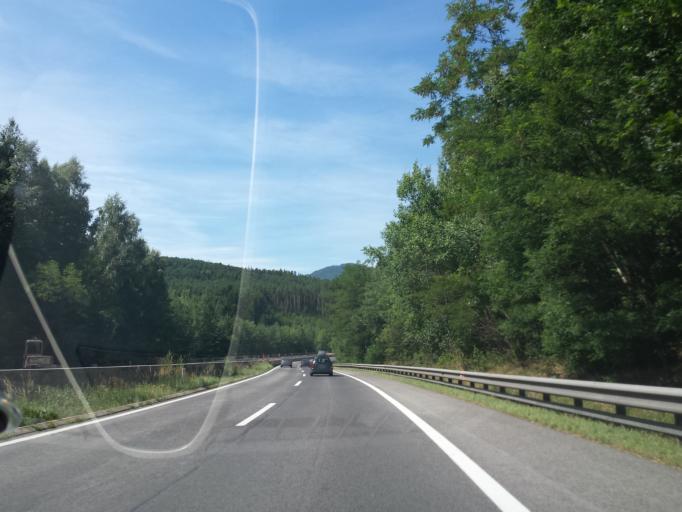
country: AT
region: Lower Austria
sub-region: Politischer Bezirk Neunkirchen
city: Enzenreith
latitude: 47.6687
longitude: 15.9730
